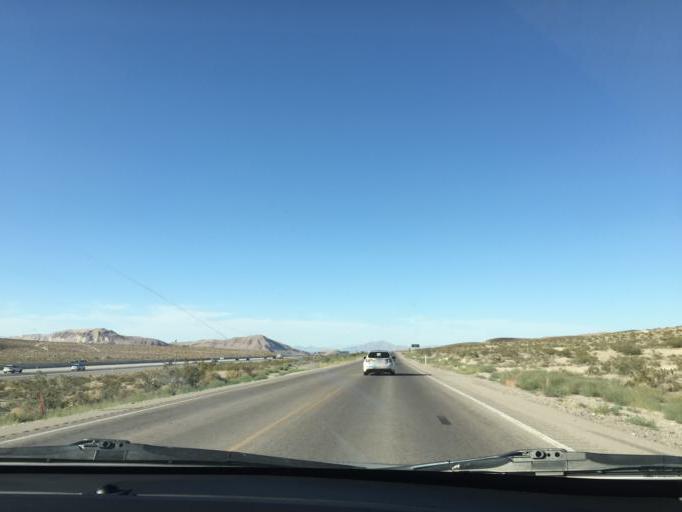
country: US
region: Nevada
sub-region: Clark County
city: Enterprise
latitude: 35.8963
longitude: -115.2161
